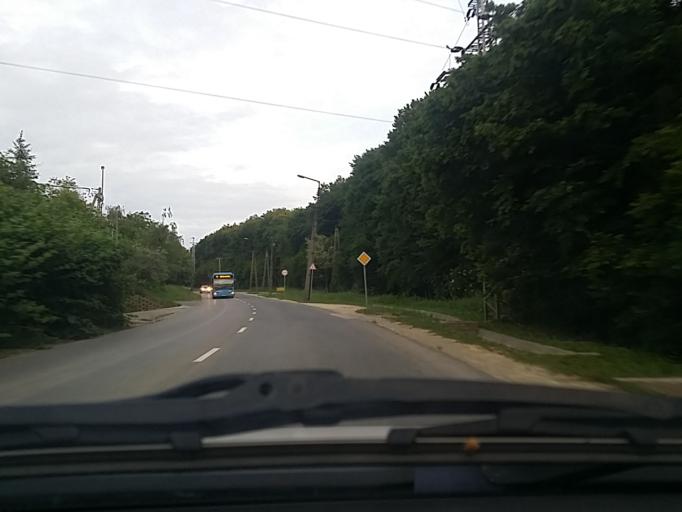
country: HU
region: Pest
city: Solymar
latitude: 47.5708
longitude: 18.9457
